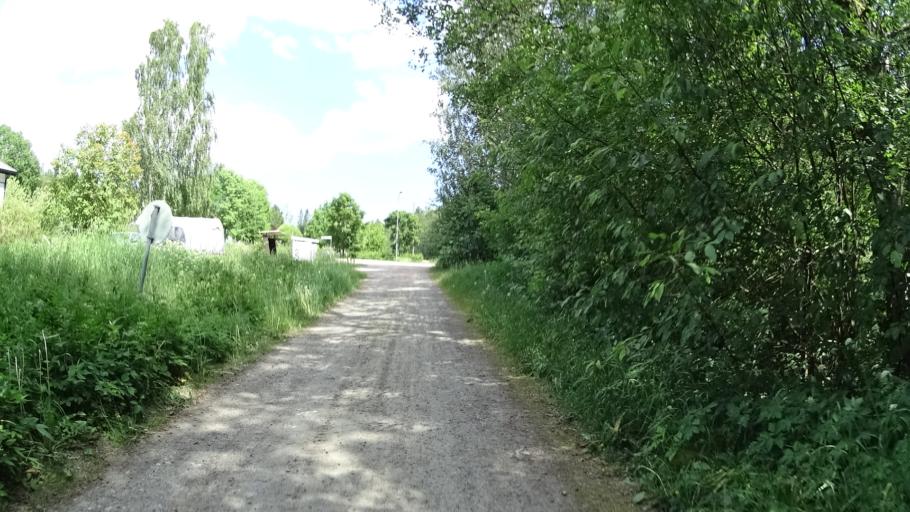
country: FI
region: Uusimaa
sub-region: Raaseporin
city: Pohja
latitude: 60.1038
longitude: 23.5563
